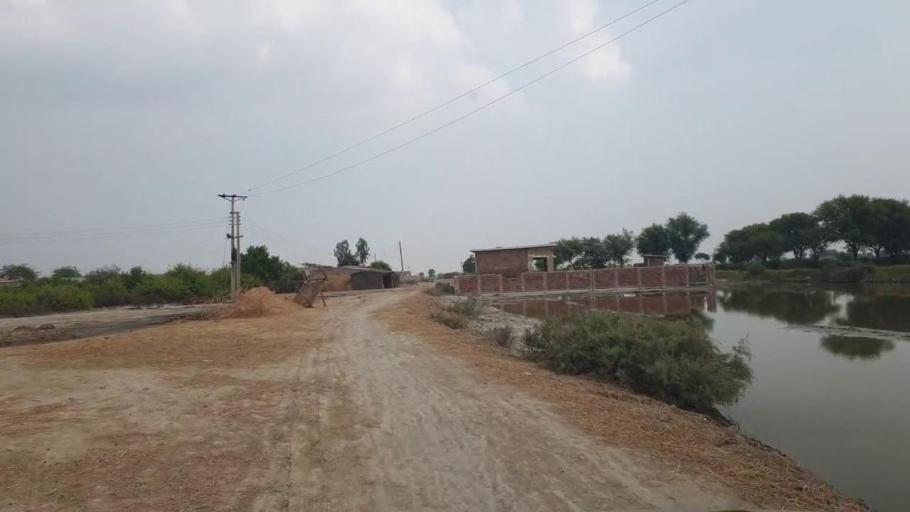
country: PK
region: Sindh
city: Matli
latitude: 24.9656
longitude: 68.7203
